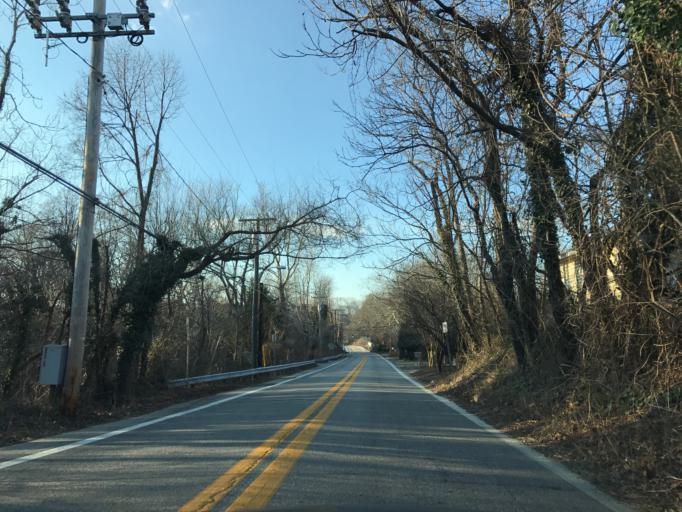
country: US
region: Maryland
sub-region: Anne Arundel County
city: Annapolis
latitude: 38.9909
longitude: -76.5053
